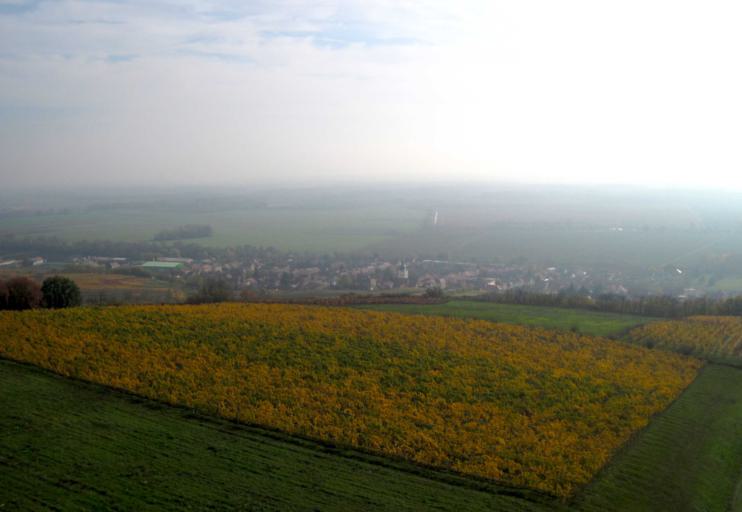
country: CZ
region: South Moravian
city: Zajeci
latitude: 48.8638
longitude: 16.7712
